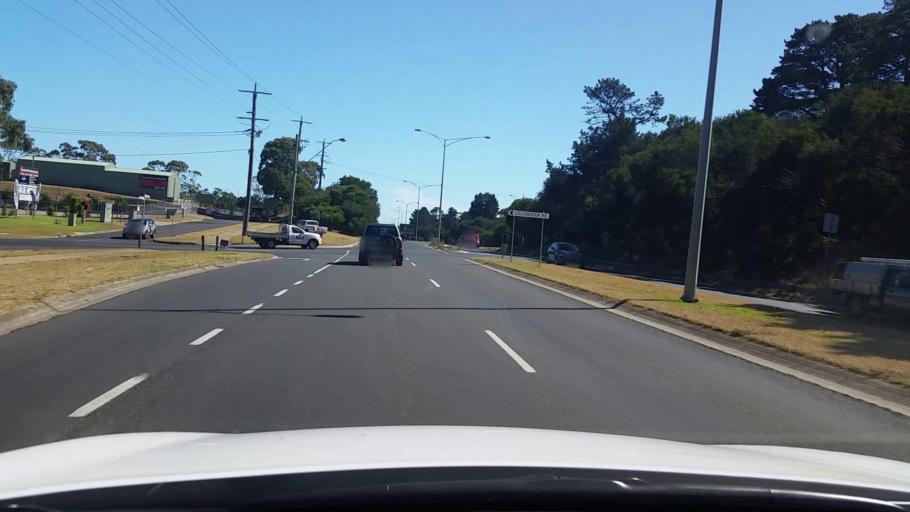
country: AU
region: Victoria
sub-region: Mornington Peninsula
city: Rosebud West
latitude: -38.3798
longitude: 144.8889
